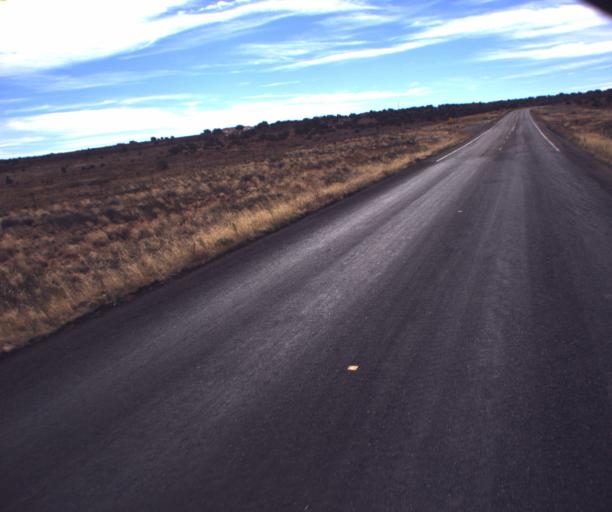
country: US
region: Arizona
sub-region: Coconino County
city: Kaibito
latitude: 36.6858
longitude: -111.2567
